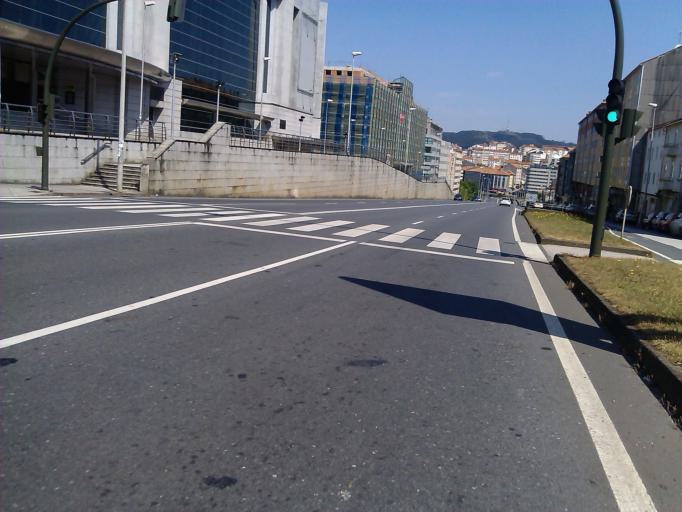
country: ES
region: Galicia
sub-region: Provincia da Coruna
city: Santiago de Compostela
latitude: 42.8626
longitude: -8.5418
